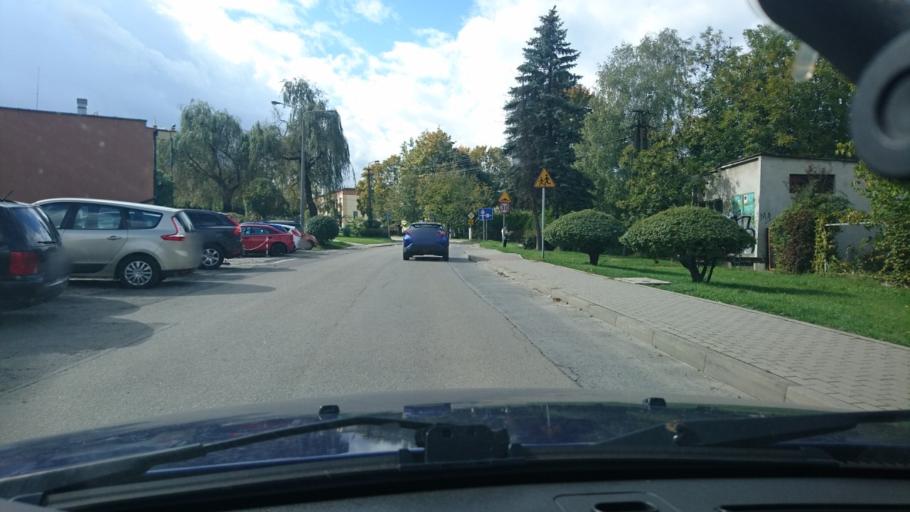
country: PL
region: Silesian Voivodeship
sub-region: Bielsko-Biala
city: Bielsko-Biala
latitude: 49.8271
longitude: 19.0312
